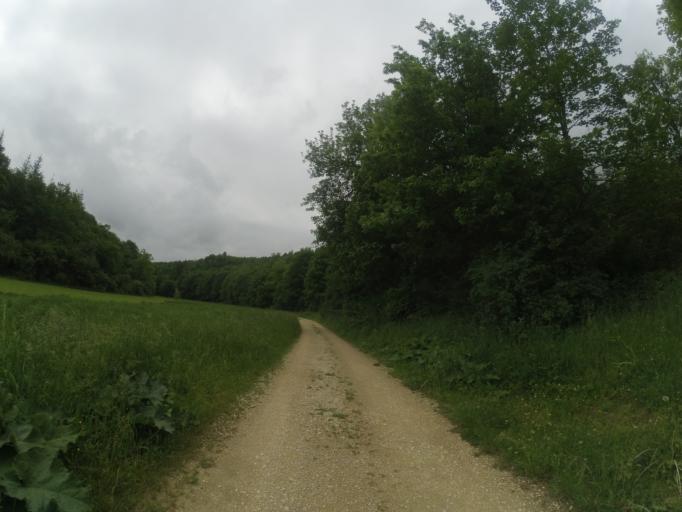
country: DE
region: Baden-Wuerttemberg
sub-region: Tuebingen Region
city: Bernstadt
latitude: 48.5187
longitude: 10.0393
